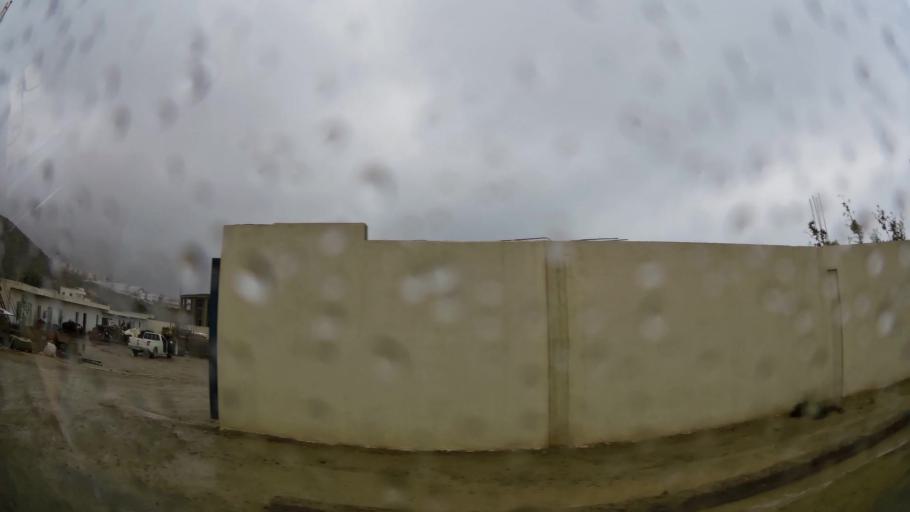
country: MA
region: Taza-Al Hoceima-Taounate
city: Al Hoceima
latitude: 35.2558
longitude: -3.9420
